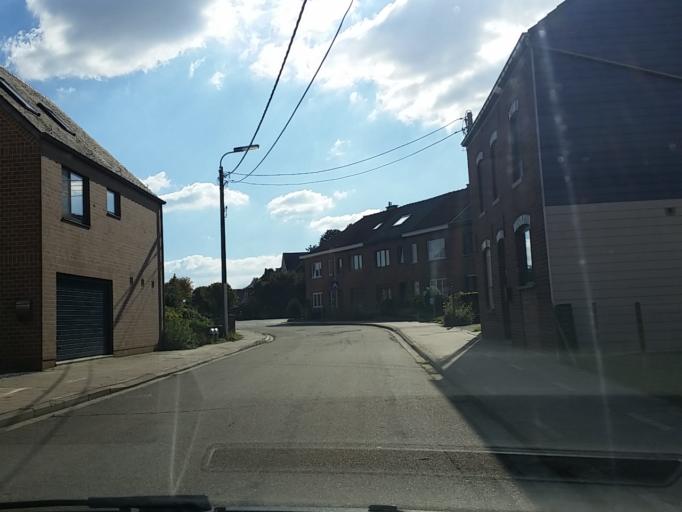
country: BE
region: Flanders
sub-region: Provincie Vlaams-Brabant
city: Rotselaar
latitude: 50.9338
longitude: 4.6976
